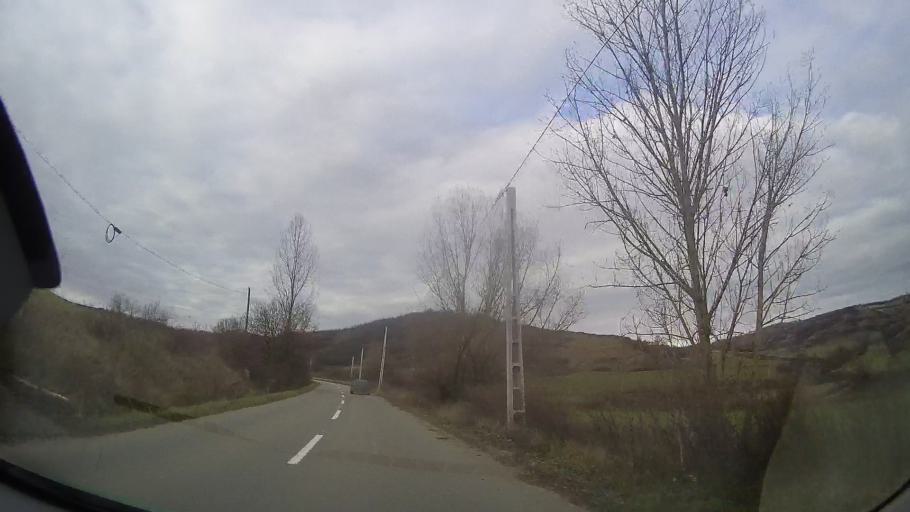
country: RO
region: Bistrita-Nasaud
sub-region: Comuna Milas
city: Milas
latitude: 46.8378
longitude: 24.4461
